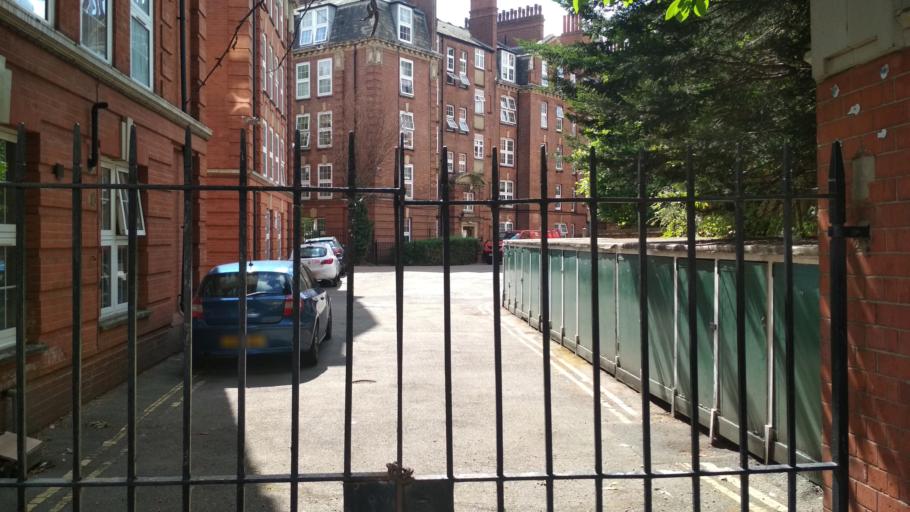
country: GB
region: England
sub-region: Greater London
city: Chelsea
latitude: 51.4913
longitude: -0.1684
